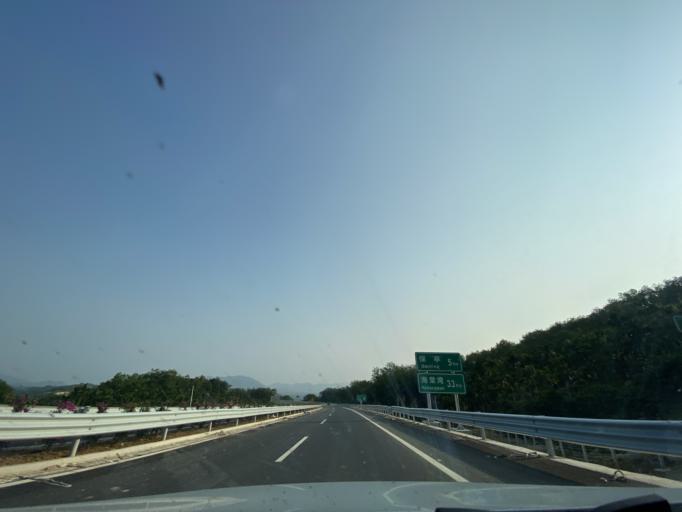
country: CN
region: Hainan
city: Xiangshui
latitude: 18.6439
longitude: 109.6292
